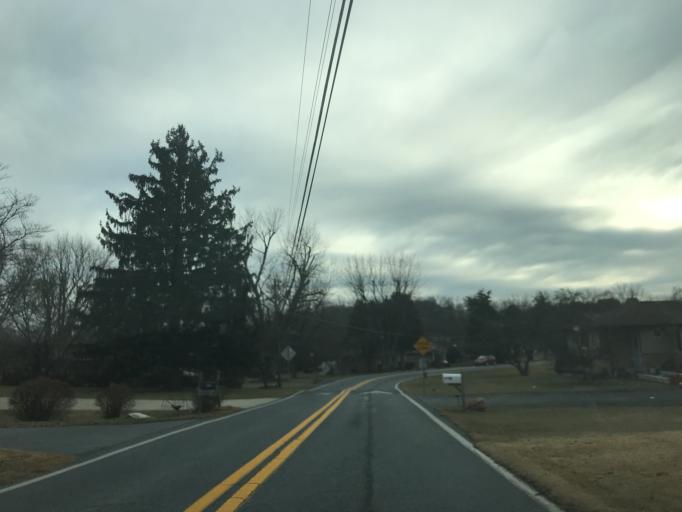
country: US
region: Maryland
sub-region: Carroll County
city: Eldersburg
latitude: 39.3924
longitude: -76.9269
